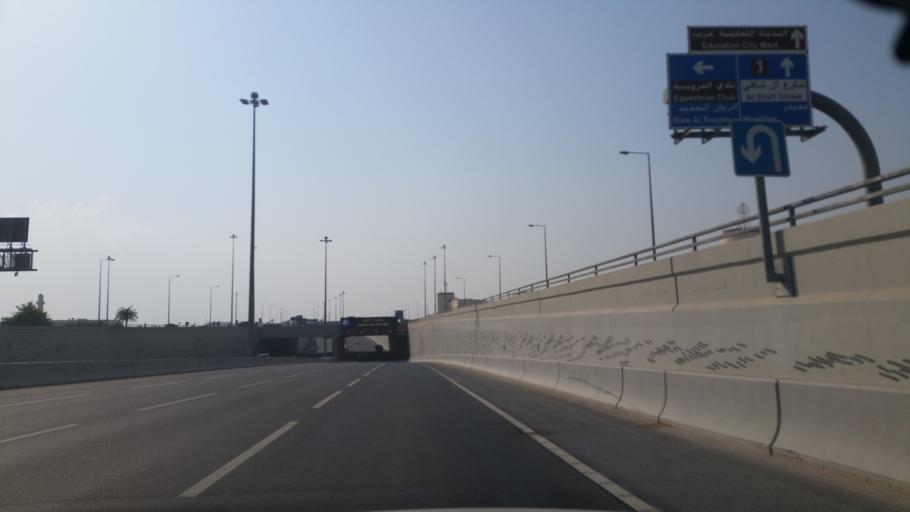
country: QA
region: Baladiyat ar Rayyan
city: Ar Rayyan
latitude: 25.2999
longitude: 51.4329
